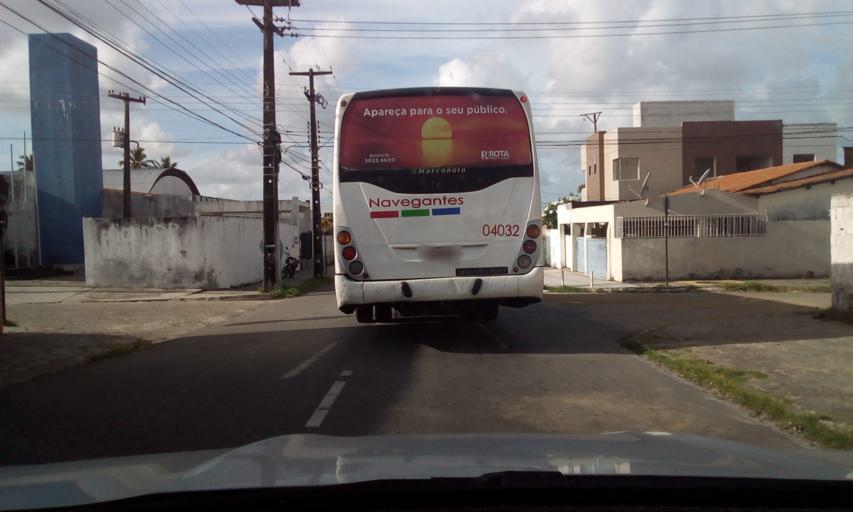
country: BR
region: Paraiba
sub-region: Joao Pessoa
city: Joao Pessoa
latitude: -7.1063
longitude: -34.8582
